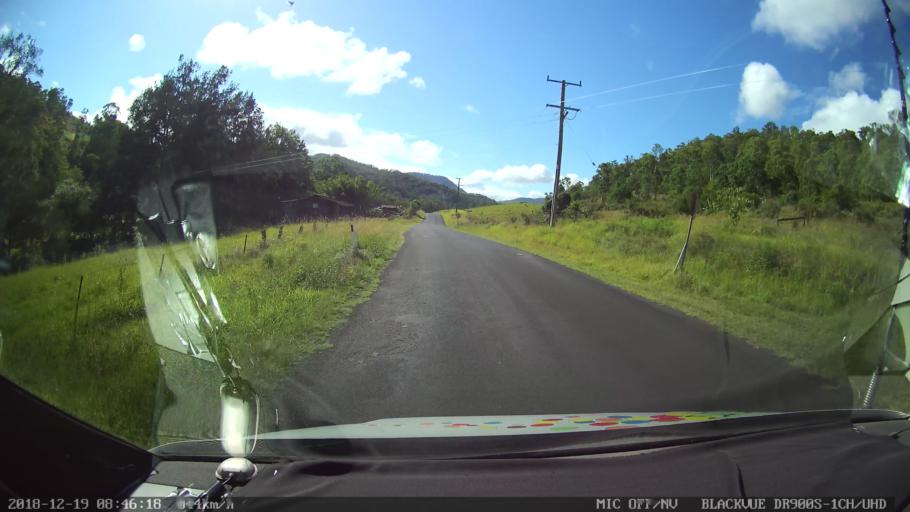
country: AU
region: New South Wales
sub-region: Kyogle
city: Kyogle
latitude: -28.3607
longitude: 152.9680
